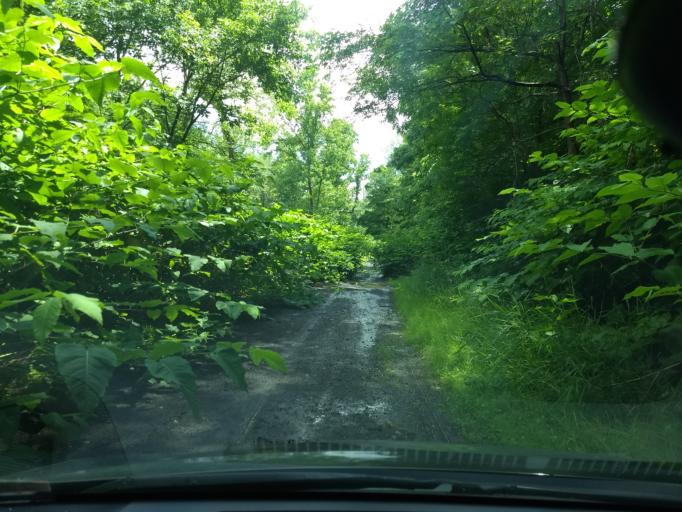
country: US
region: Pennsylvania
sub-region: Westmoreland County
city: Avonmore
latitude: 40.5297
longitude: -79.4990
